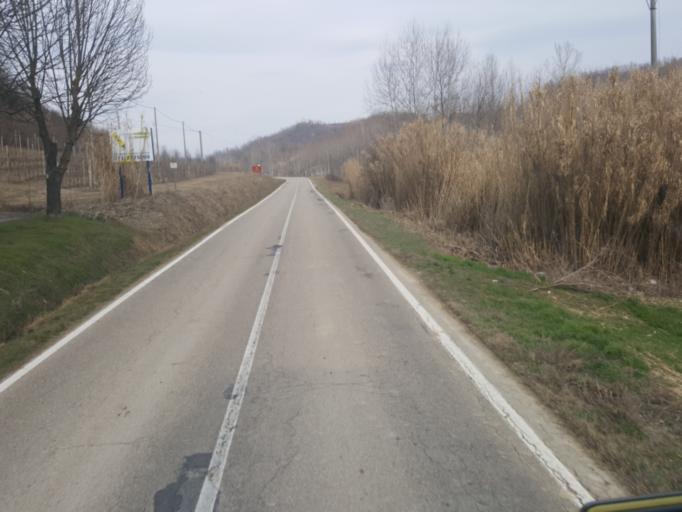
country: IT
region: Piedmont
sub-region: Provincia di Asti
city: Castelnuovo Belbo
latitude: 44.7862
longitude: 8.4175
